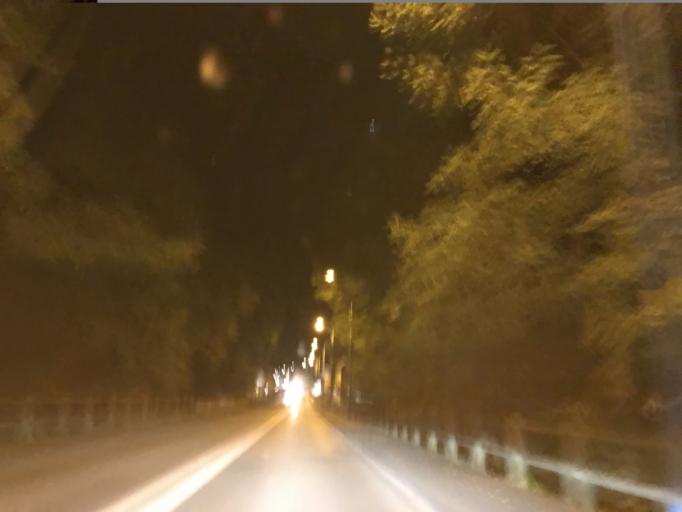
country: FR
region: Auvergne
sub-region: Departement du Puy-de-Dome
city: Puy-Guillaume
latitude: 45.9634
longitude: 3.4757
